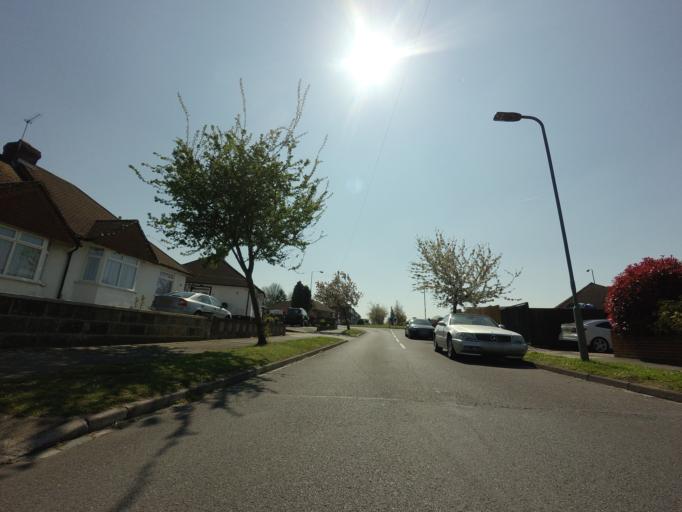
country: GB
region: England
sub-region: Greater London
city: Orpington
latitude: 51.3784
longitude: 0.1104
